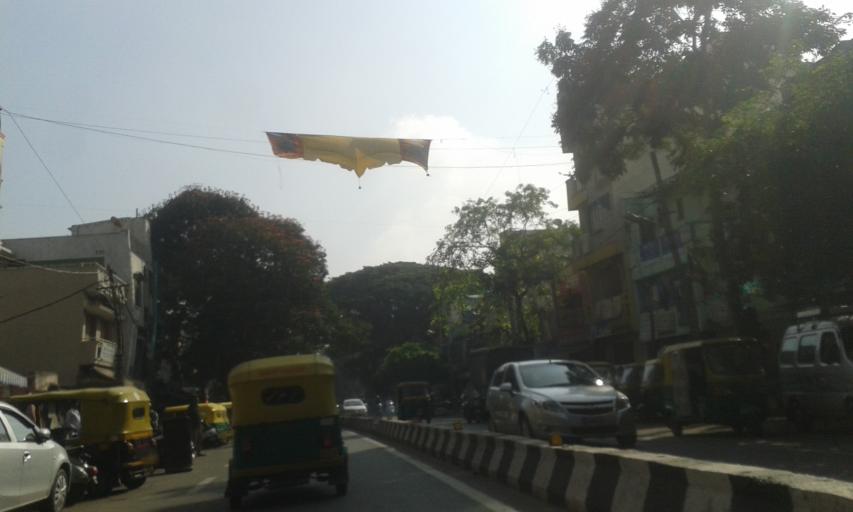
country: IN
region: Karnataka
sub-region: Bangalore Urban
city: Bangalore
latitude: 12.9285
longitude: 77.5944
